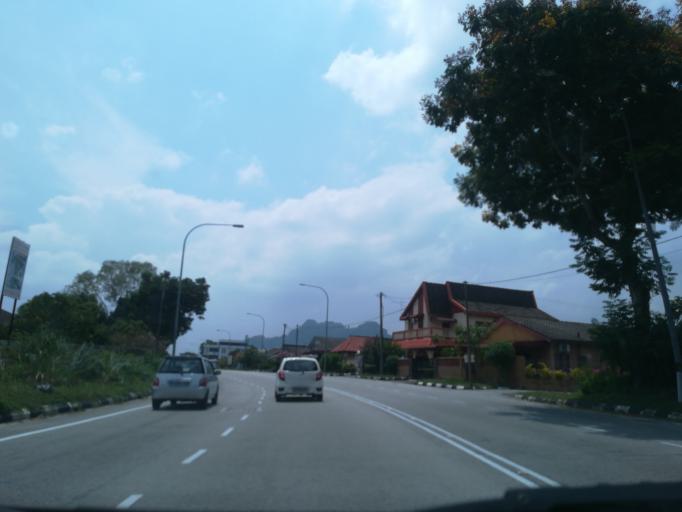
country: MY
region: Perak
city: Ipoh
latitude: 4.5743
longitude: 101.1272
